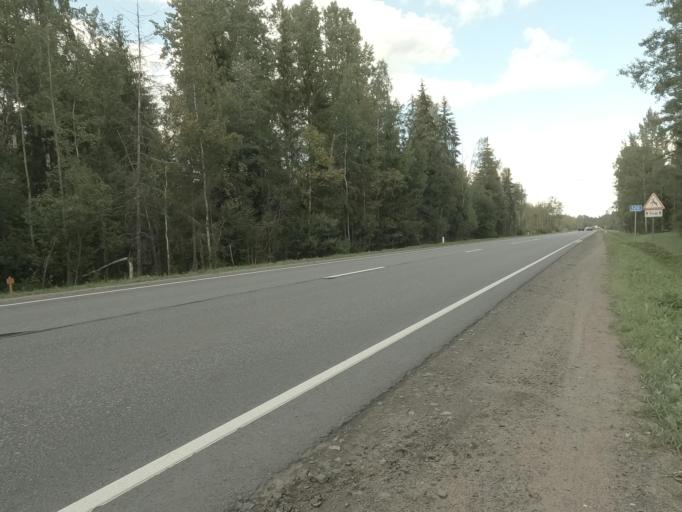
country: RU
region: Leningrad
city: Pavlovo
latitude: 59.6771
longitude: 30.9333
